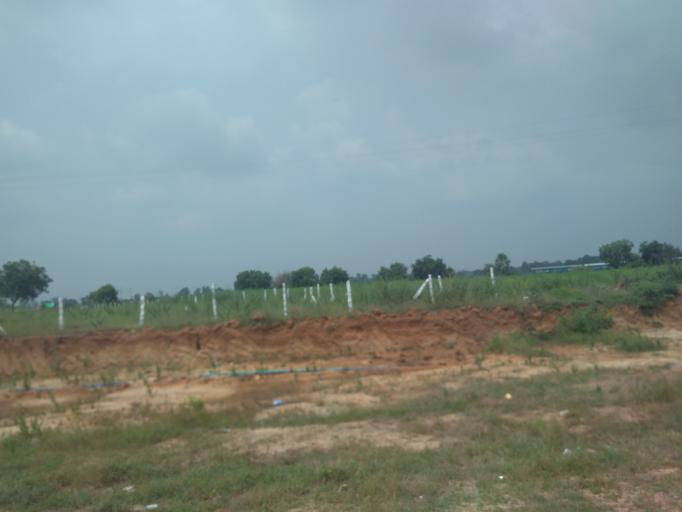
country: IN
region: Telangana
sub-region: Warangal
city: Jangaon
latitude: 17.6638
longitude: 79.0836
